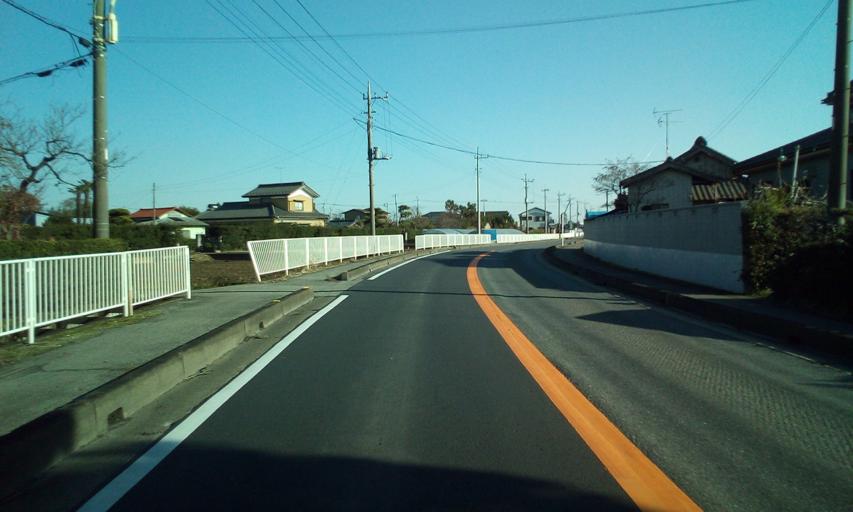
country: JP
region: Saitama
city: Yoshikawa
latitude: 35.8990
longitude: 139.8698
